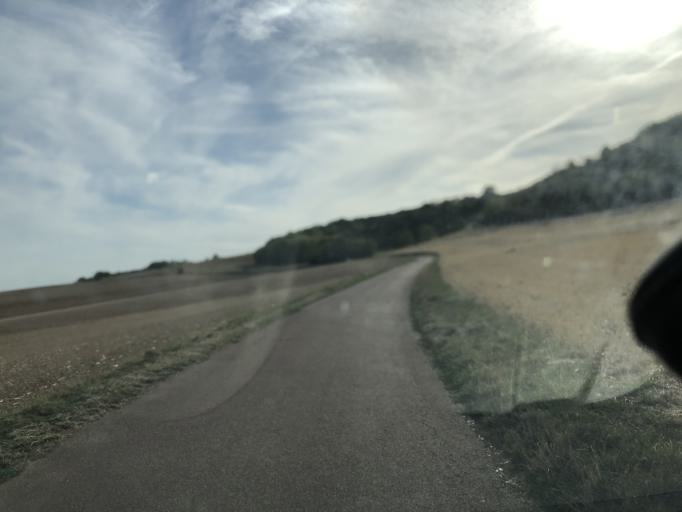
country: FR
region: Bourgogne
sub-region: Departement de l'Yonne
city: Joigny
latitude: 47.9404
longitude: 3.3908
